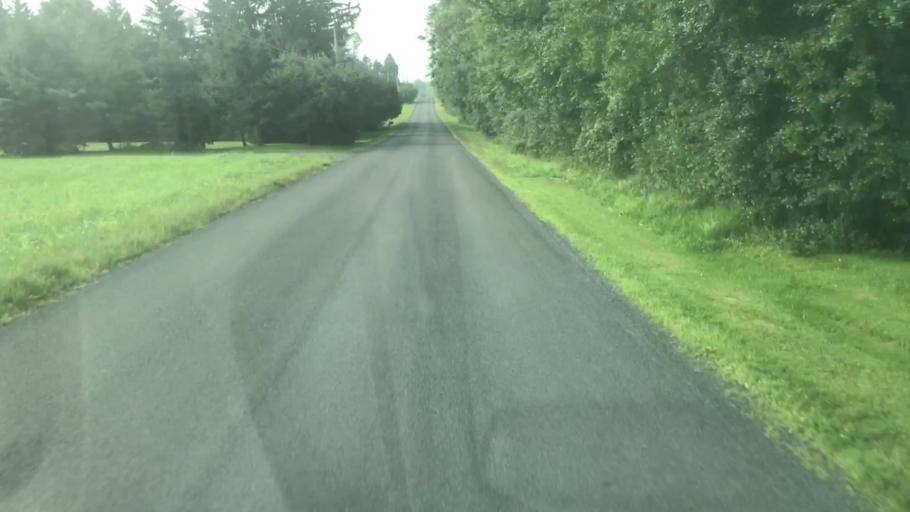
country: US
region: New York
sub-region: Onondaga County
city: Skaneateles
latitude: 42.9218
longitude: -76.4568
